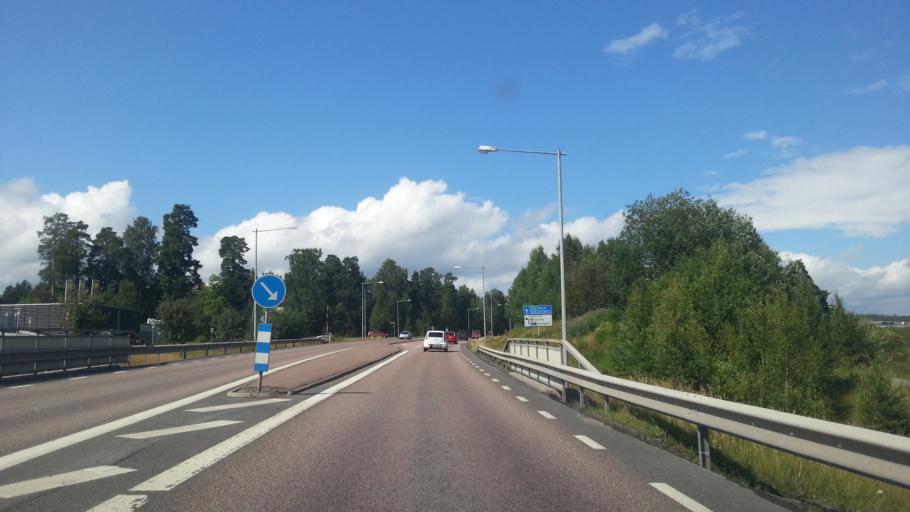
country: SE
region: Dalarna
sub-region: Faluns Kommun
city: Falun
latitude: 60.6087
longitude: 15.6575
